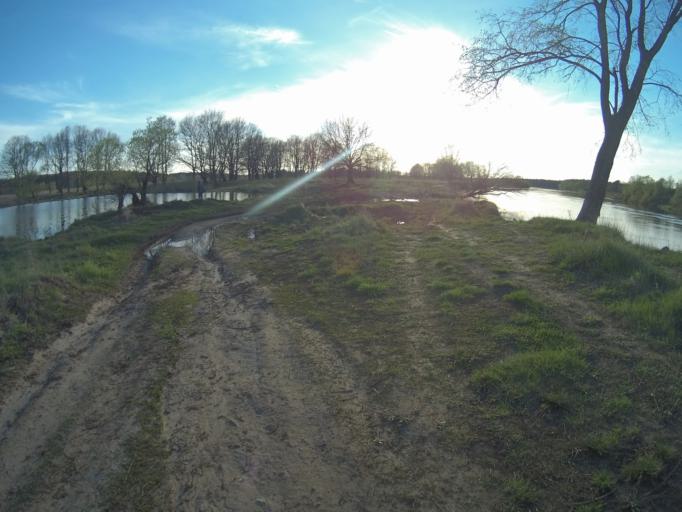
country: RU
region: Vladimir
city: Raduzhnyy
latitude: 56.0328
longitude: 40.2759
